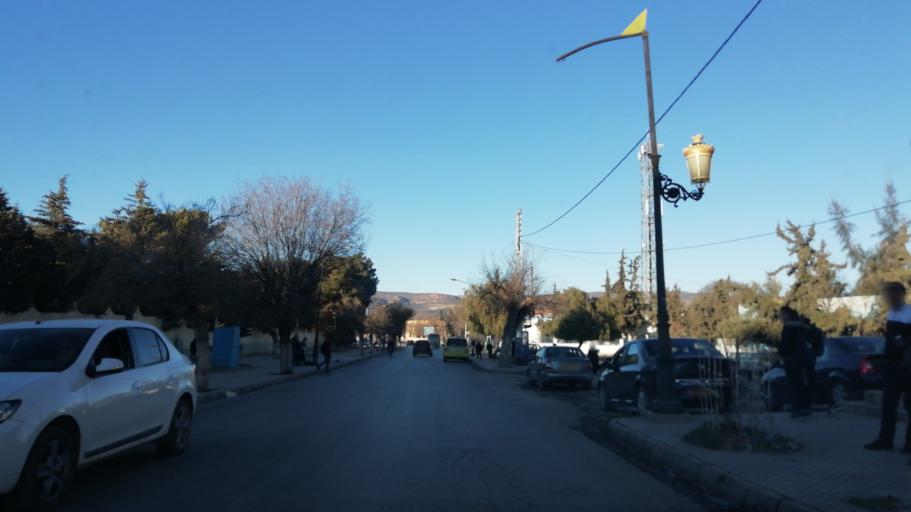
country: DZ
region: Tlemcen
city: Sebdou
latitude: 34.6359
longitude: -1.3333
